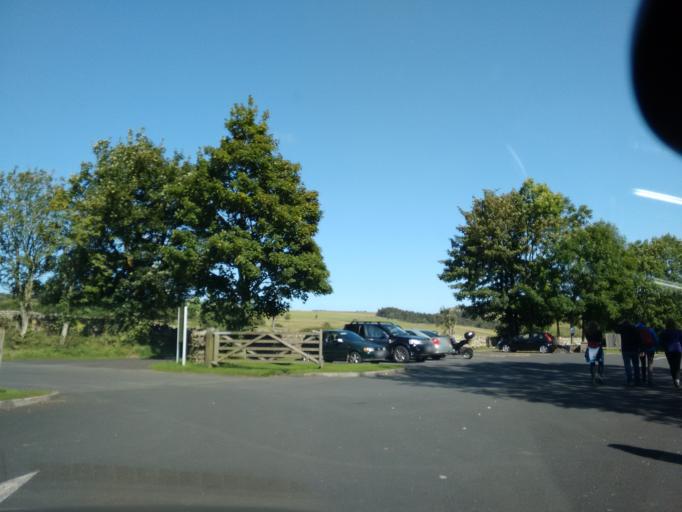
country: GB
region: England
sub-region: Northumberland
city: Bardon Mill
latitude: 54.9913
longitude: -2.3658
